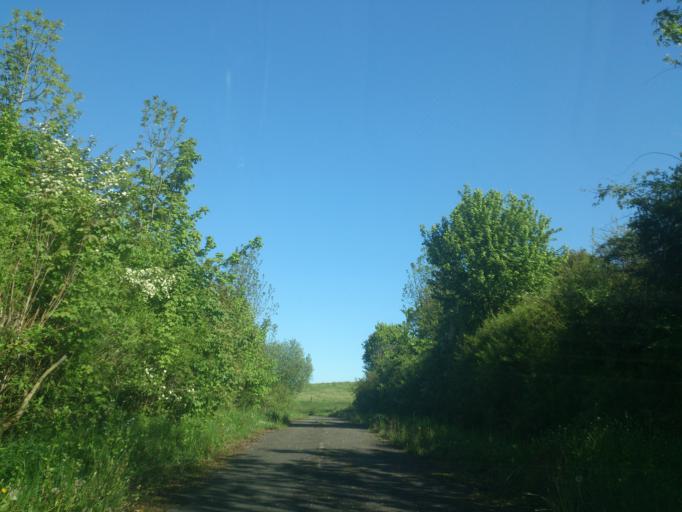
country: DE
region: North Rhine-Westphalia
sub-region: Regierungsbezirk Detmold
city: Willebadessen
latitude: 51.6650
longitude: 9.0064
